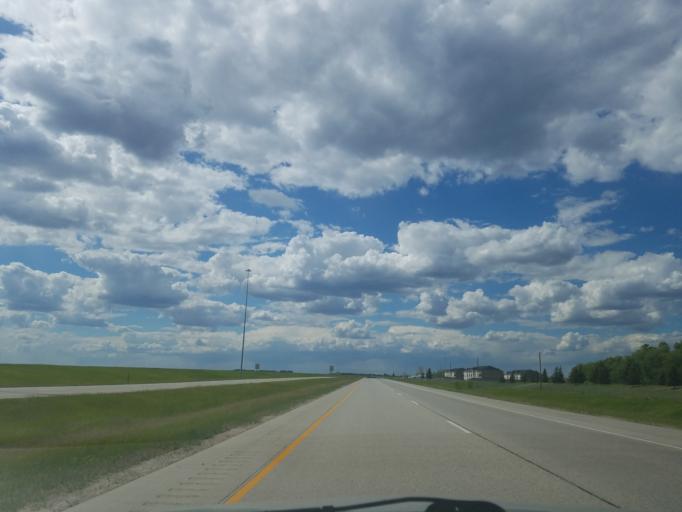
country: US
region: North Dakota
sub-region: Cass County
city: West Fargo
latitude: 46.8562
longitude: -96.9174
